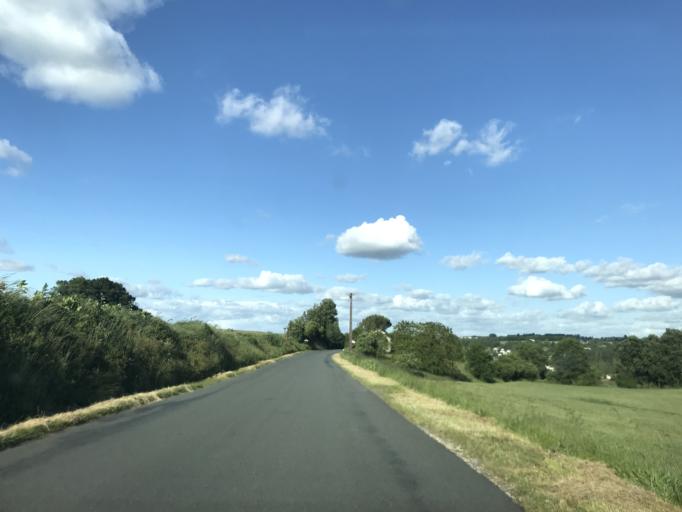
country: FR
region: Poitou-Charentes
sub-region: Departement de la Charente
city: Chalais
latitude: 45.2706
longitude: 0.0255
